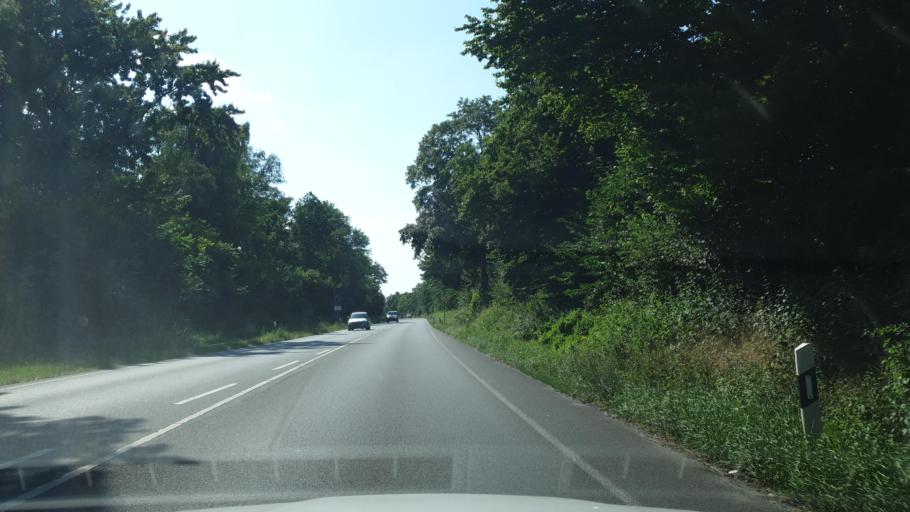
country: DE
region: North Rhine-Westphalia
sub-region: Regierungsbezirk Detmold
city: Herford
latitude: 52.1307
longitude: 8.6857
